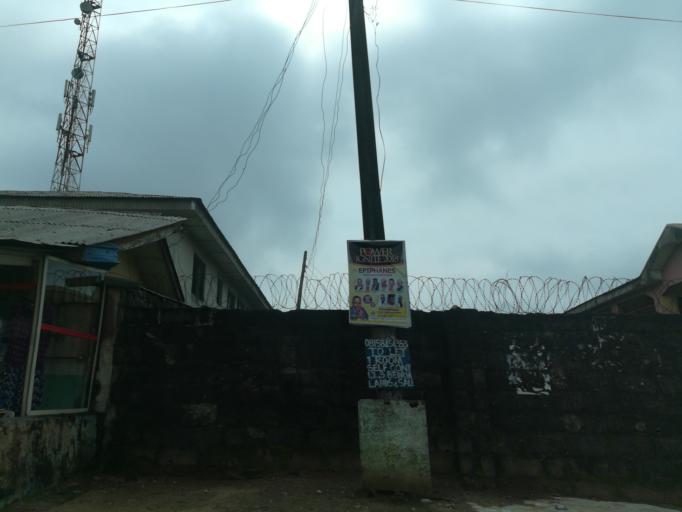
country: NG
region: Rivers
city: Port Harcourt
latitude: 4.8764
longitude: 6.9804
